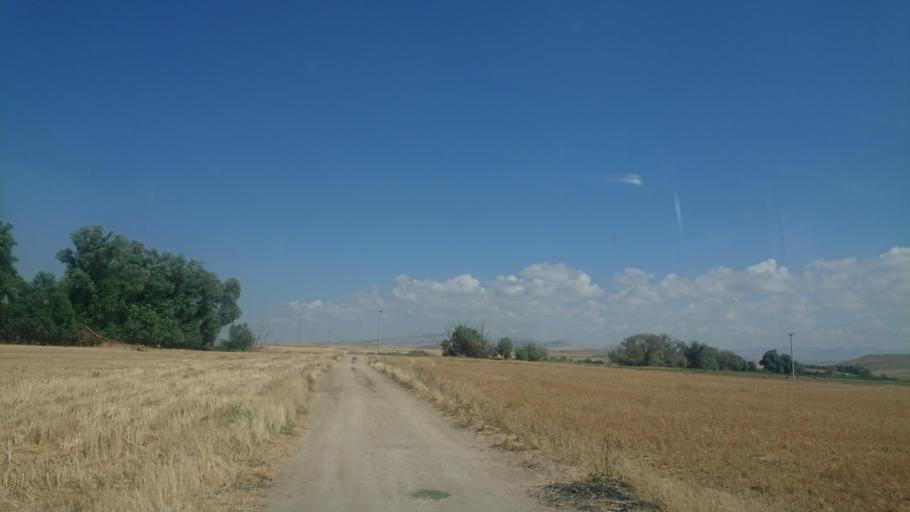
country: TR
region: Aksaray
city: Sariyahsi
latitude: 38.9967
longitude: 33.8946
